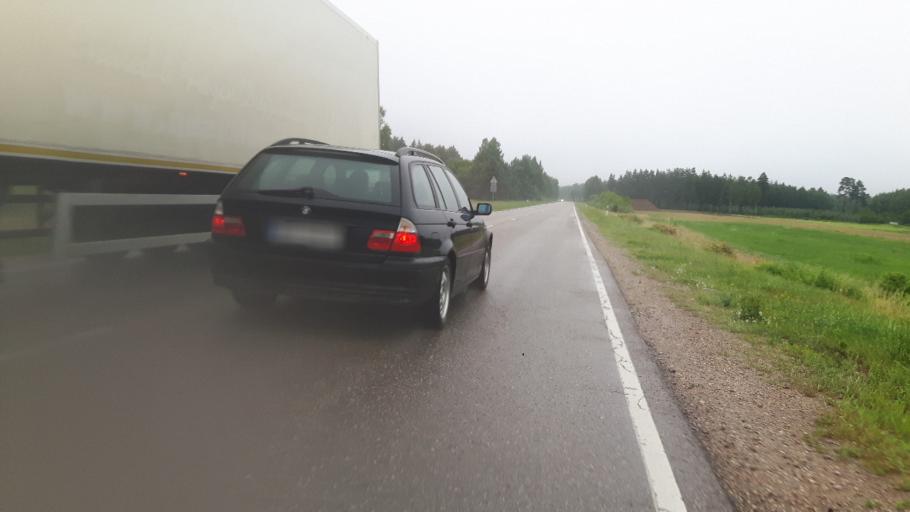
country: LV
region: Rucavas
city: Rucava
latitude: 56.1021
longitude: 21.1345
